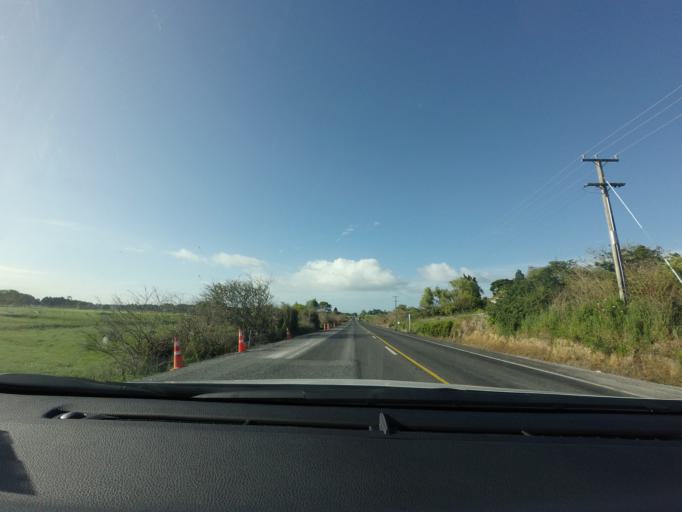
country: NZ
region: Waikato
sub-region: Hauraki District
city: Ngatea
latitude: -37.4632
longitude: 175.5104
